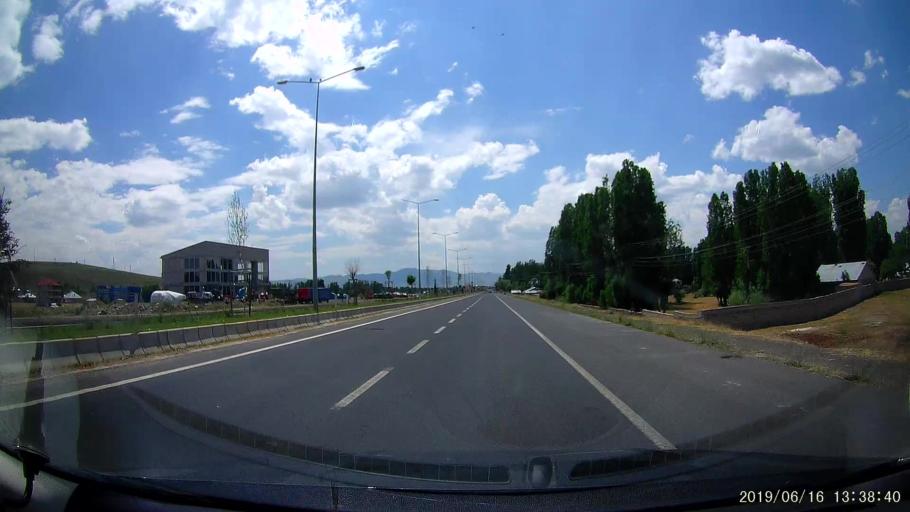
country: TR
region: Agri
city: Agri
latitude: 39.7107
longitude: 43.0708
